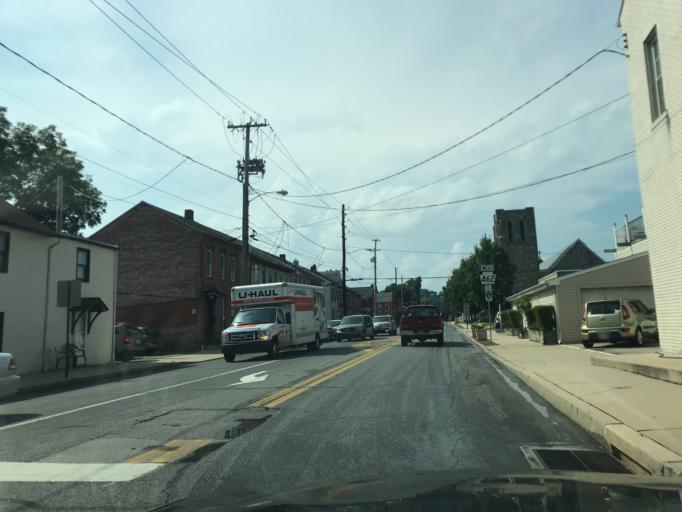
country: US
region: Pennsylvania
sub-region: Lancaster County
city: Columbia
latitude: 40.0339
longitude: -76.4995
